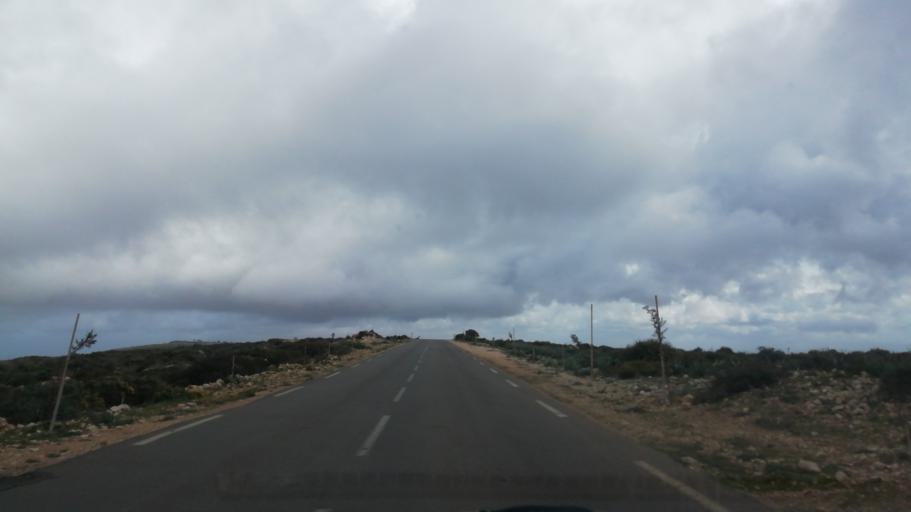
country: DZ
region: Oran
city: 'Ain el Turk
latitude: 35.6995
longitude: -0.7562
